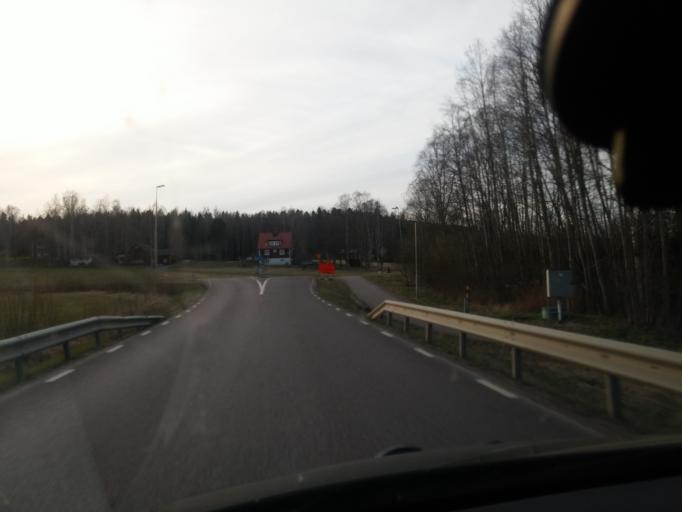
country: SE
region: Dalarna
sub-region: Borlange Kommun
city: Borlaenge
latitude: 60.5482
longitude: 15.4169
